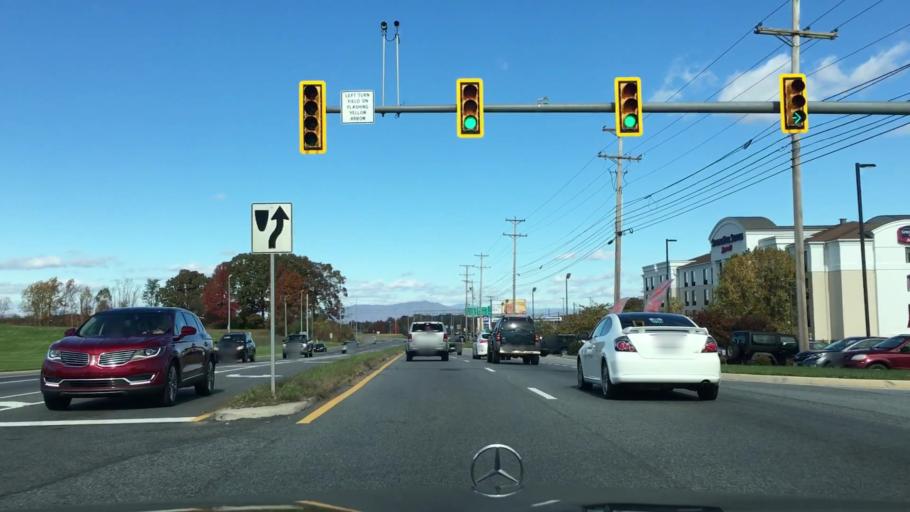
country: US
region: Virginia
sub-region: Campbell County
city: Timberlake
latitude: 37.3341
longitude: -79.1916
